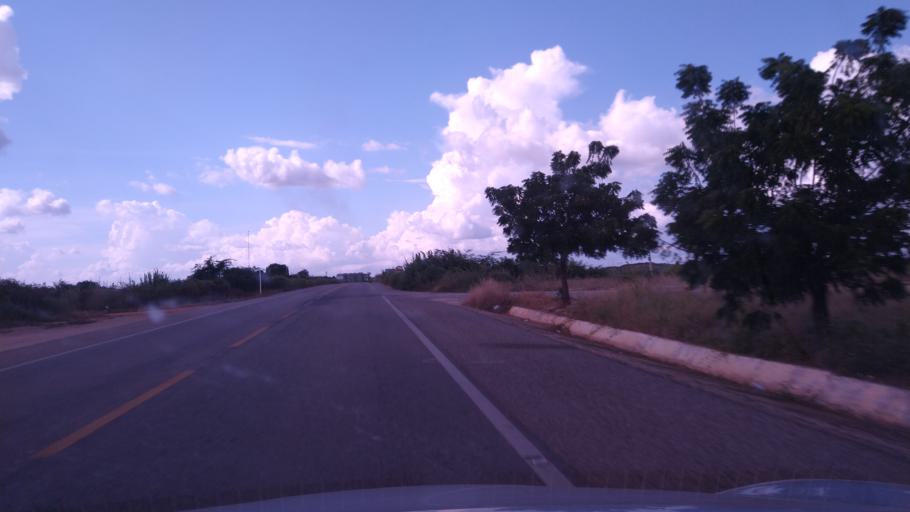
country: BR
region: Ceara
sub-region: Caninde
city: Caninde
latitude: -4.3898
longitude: -39.3133
